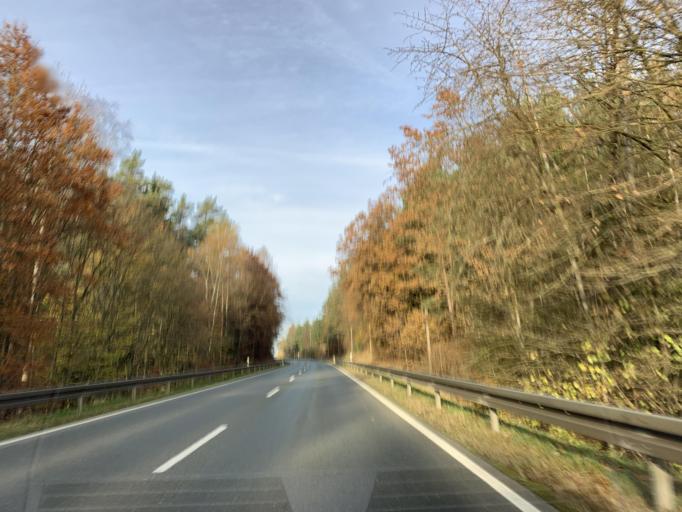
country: DE
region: Bavaria
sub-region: Upper Palatinate
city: Thanstein
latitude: 49.3513
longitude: 12.4350
